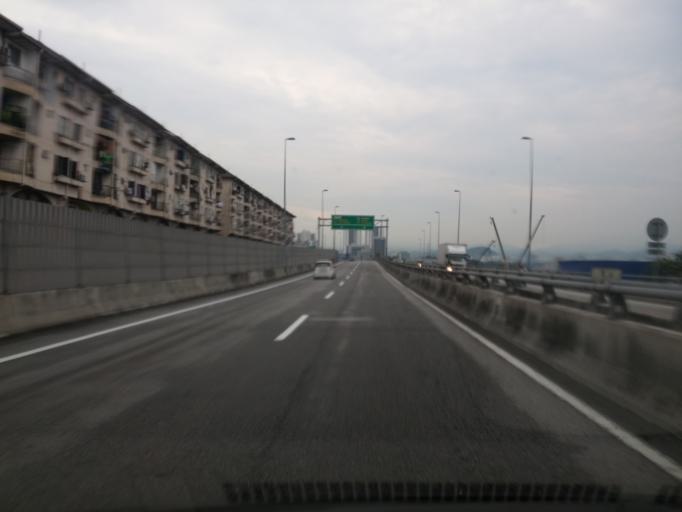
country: MY
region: Kuala Lumpur
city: Kuala Lumpur
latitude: 3.1327
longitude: 101.7187
